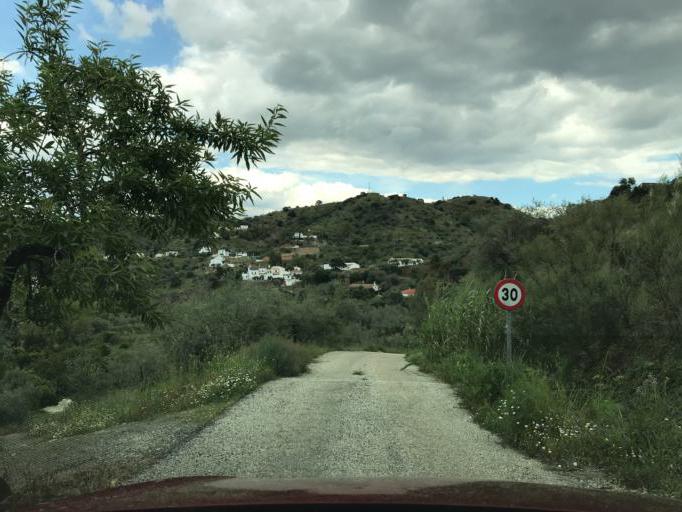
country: ES
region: Andalusia
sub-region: Provincia de Malaga
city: Comares
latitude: 36.8777
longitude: -4.2611
